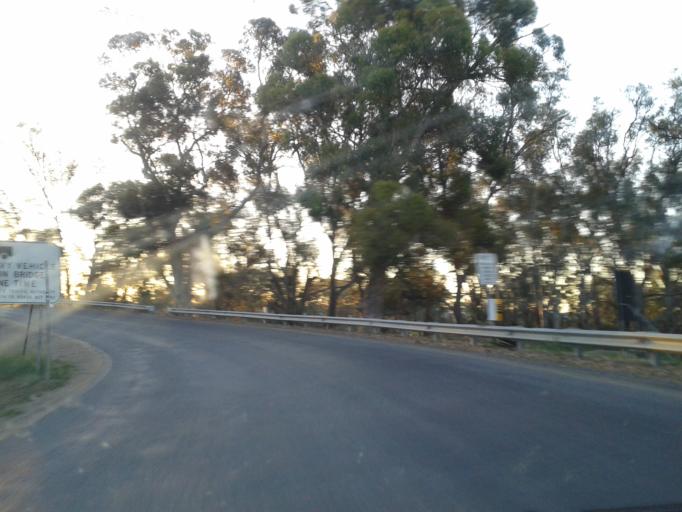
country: AU
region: Victoria
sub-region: Swan Hill
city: Swan Hill
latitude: -35.3373
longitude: 143.5641
